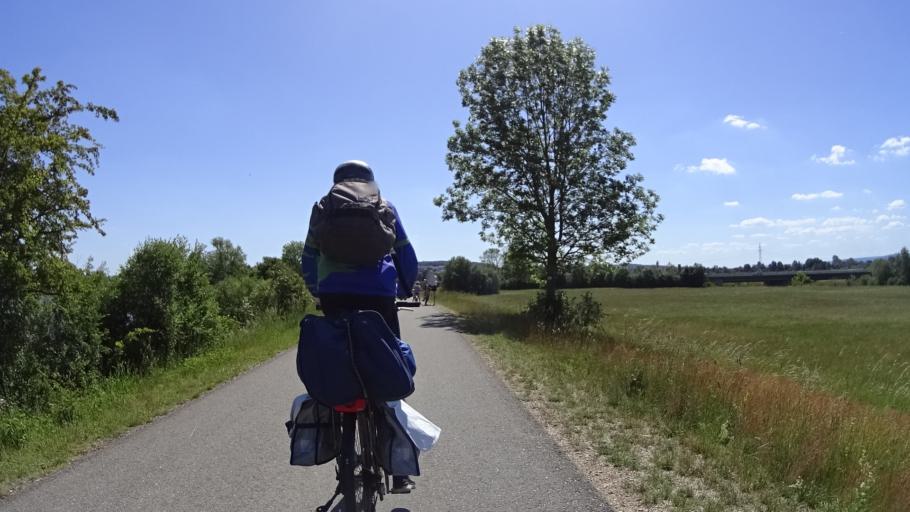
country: DE
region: Bavaria
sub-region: Regierungsbezirk Mittelfranken
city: Gunzenhausen
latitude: 49.1235
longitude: 10.7386
